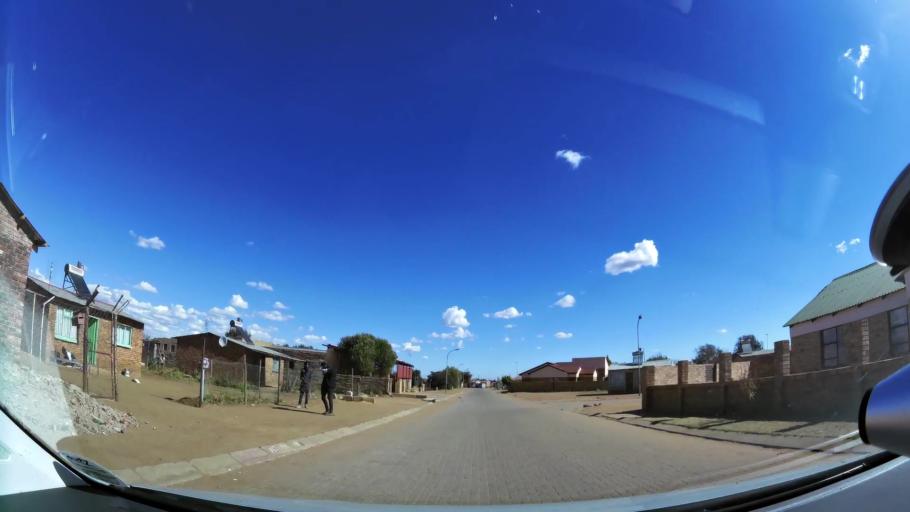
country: ZA
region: North-West
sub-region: Dr Kenneth Kaunda District Municipality
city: Klerksdorp
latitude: -26.8685
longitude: 26.5776
